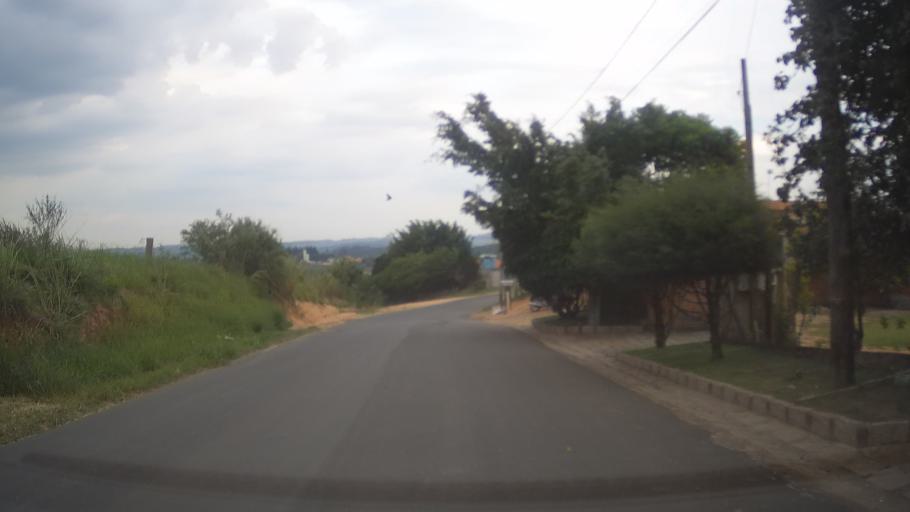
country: BR
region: Sao Paulo
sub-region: Itupeva
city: Itupeva
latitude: -23.1756
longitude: -47.0890
